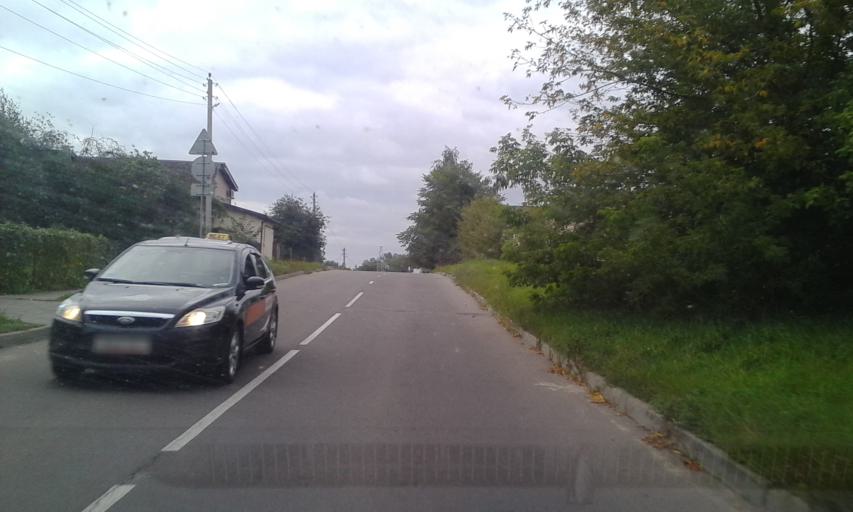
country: BY
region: Minsk
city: Minsk
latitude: 53.9430
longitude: 27.5708
